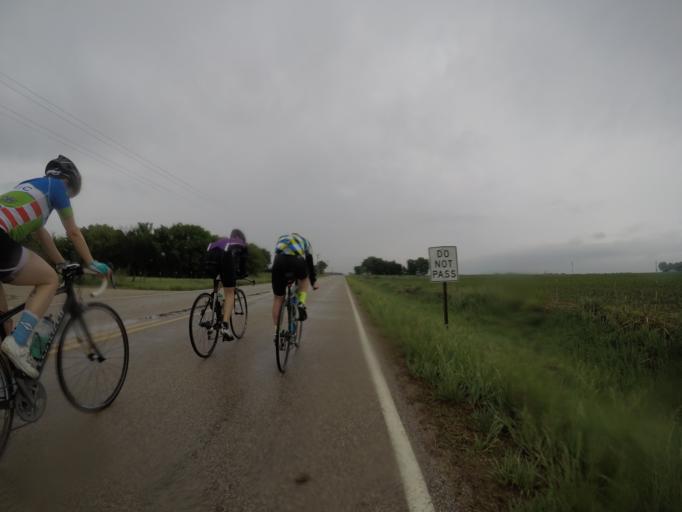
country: US
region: Kansas
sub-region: Pottawatomie County
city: Wamego
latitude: 39.3493
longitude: -96.2212
